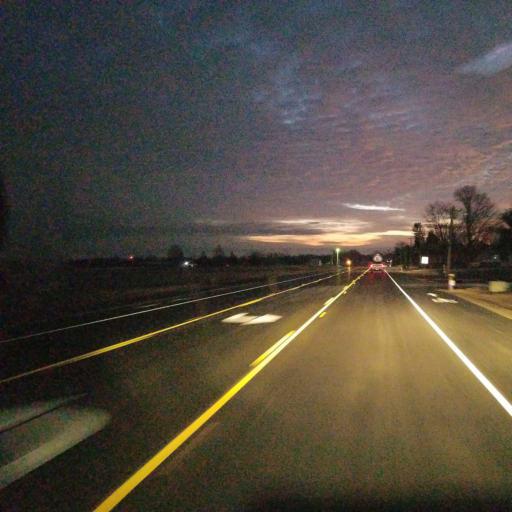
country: US
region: Illinois
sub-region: Peoria County
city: Hanna City
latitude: 40.6917
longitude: -89.7837
